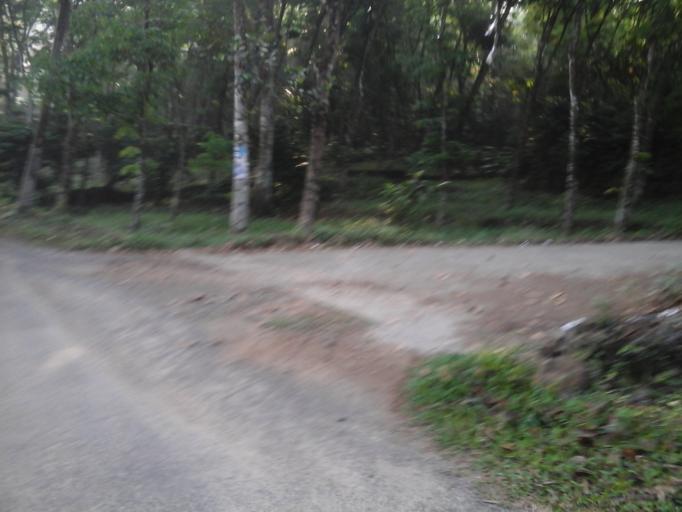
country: IN
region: Kerala
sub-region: Kottayam
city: Erattupetta
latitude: 9.5924
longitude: 76.7210
